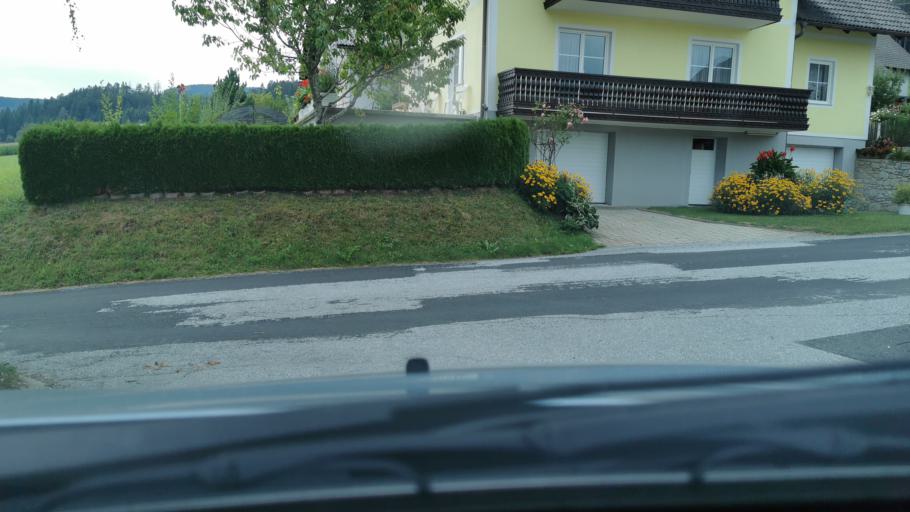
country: AT
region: Styria
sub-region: Politischer Bezirk Weiz
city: Strallegg
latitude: 47.3939
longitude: 15.6837
